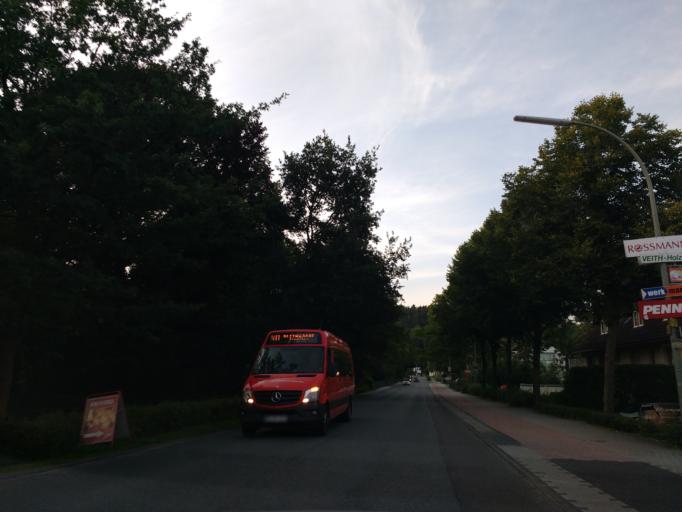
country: DE
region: North Rhine-Westphalia
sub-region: Regierungsbezirk Detmold
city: Wunnenberg
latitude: 51.5217
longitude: 8.6962
